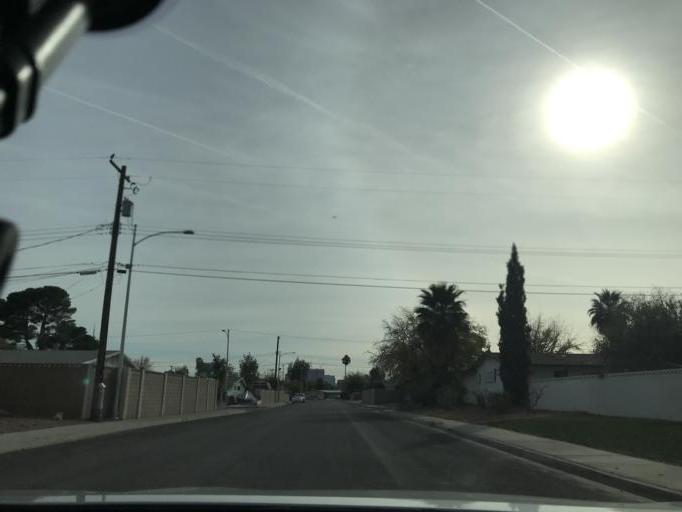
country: US
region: Nevada
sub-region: Clark County
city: Las Vegas
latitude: 36.1722
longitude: -115.1682
